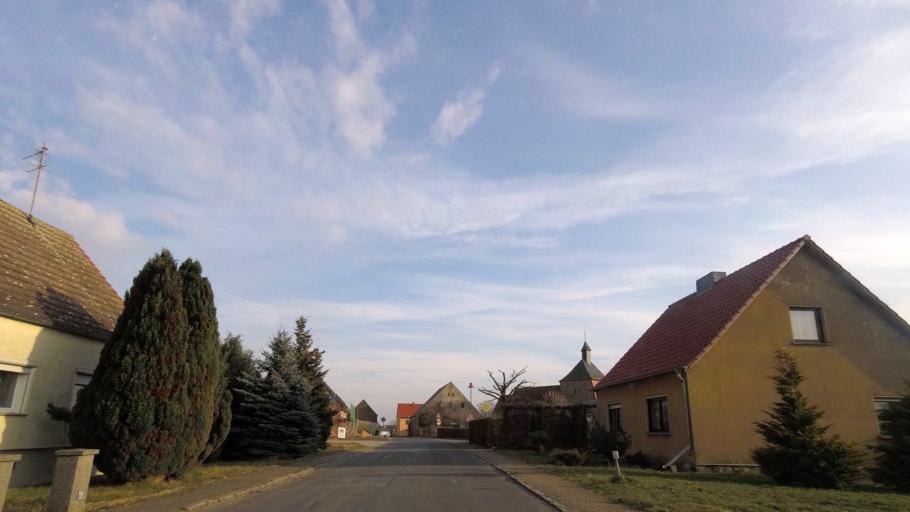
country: DE
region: Brandenburg
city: Belzig
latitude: 52.1031
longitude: 12.5524
